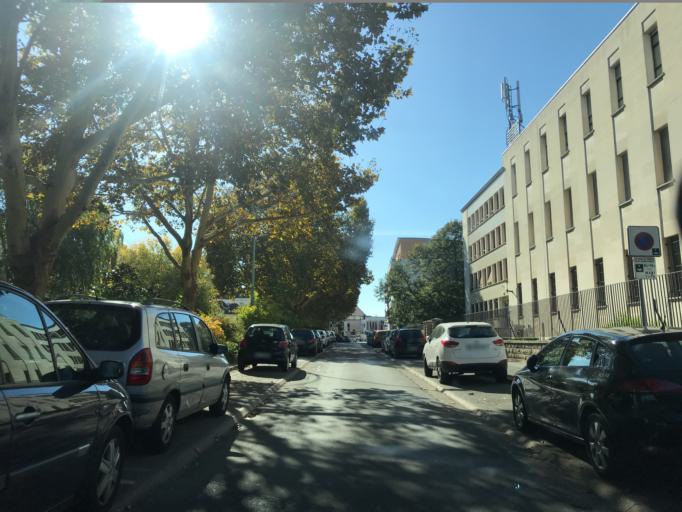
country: FR
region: Ile-de-France
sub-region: Departement du Val-d'Oise
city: Pontoise
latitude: 49.0477
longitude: 2.1078
